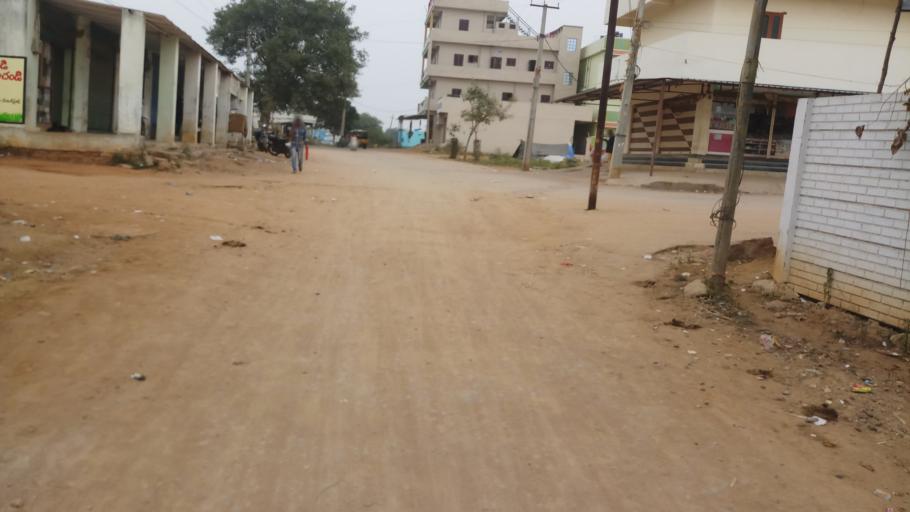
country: IN
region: Telangana
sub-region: Rangareddi
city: Quthbullapur
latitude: 17.6685
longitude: 78.4703
